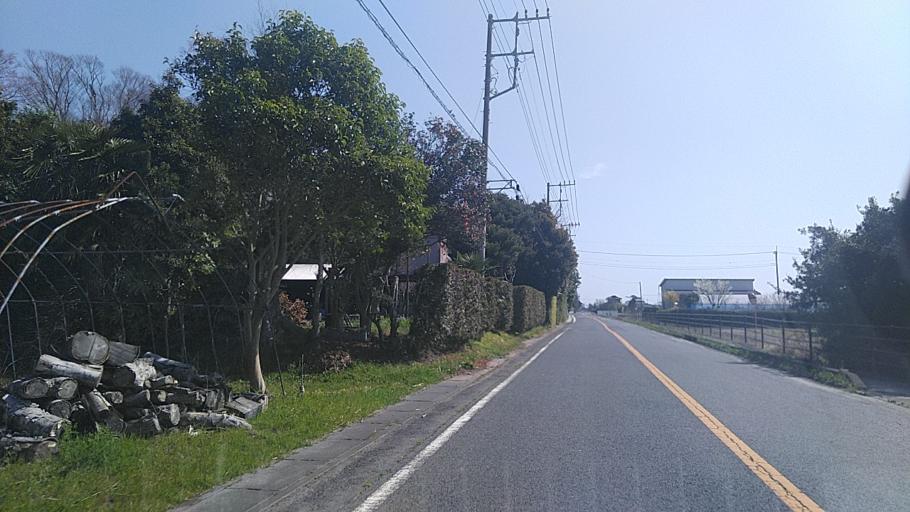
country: JP
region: Ibaraki
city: Ryugasaki
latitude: 35.8616
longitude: 140.1669
